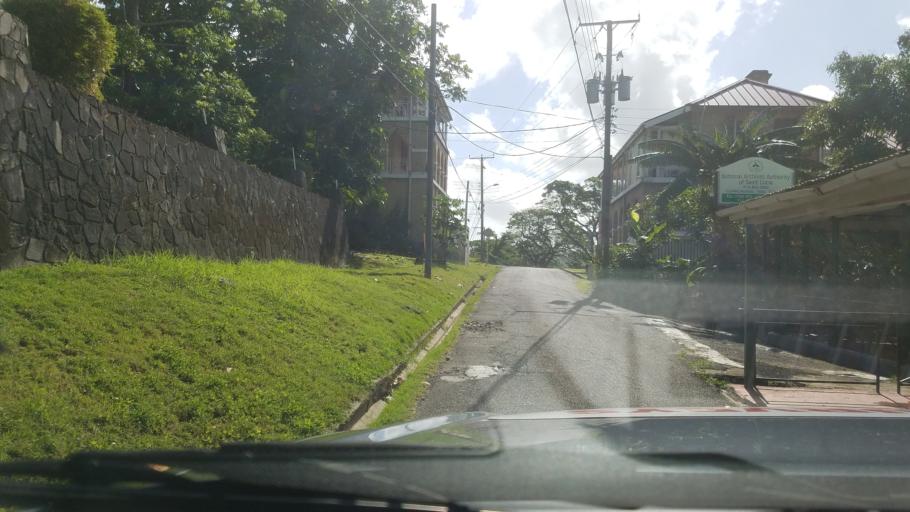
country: LC
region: Castries Quarter
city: Bisee
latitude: 14.0195
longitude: -60.9984
